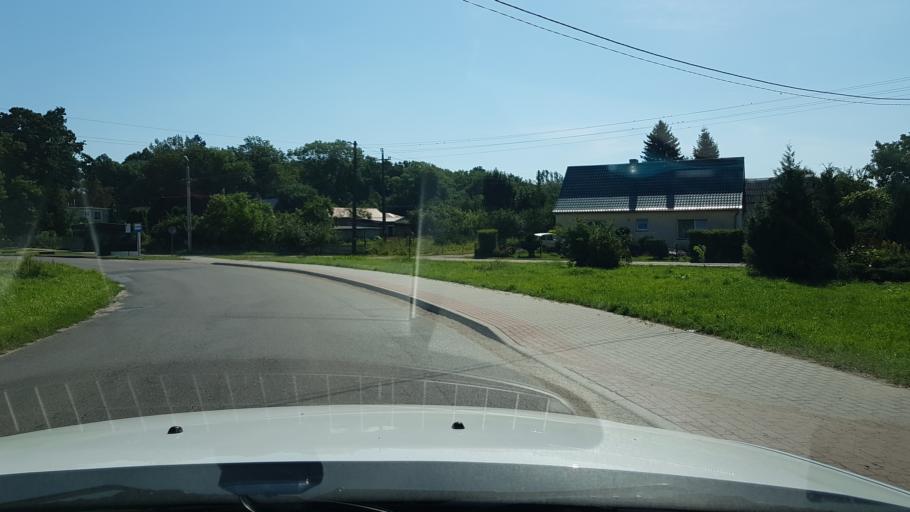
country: PL
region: West Pomeranian Voivodeship
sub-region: Powiat koszalinski
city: Sianow
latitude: 54.2447
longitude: 16.2874
